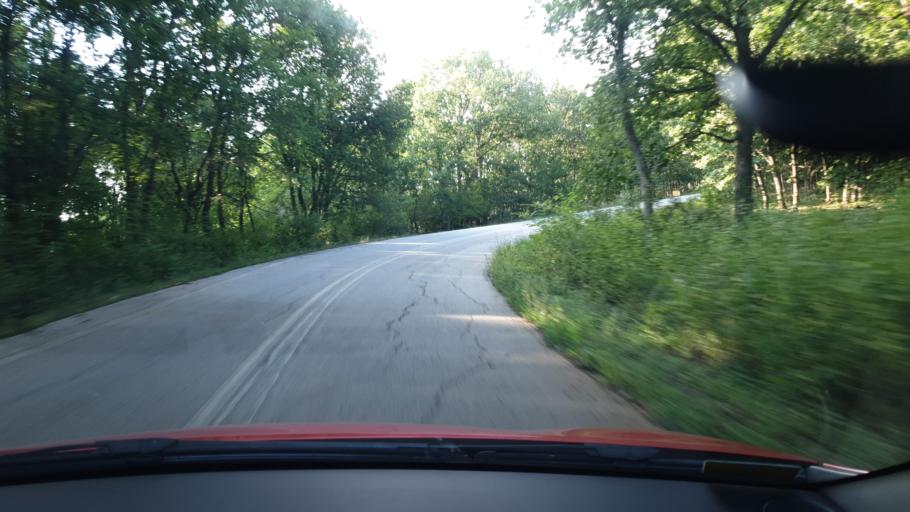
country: GR
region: Central Macedonia
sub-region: Nomos Chalkidikis
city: Galatista
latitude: 40.5379
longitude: 23.2777
